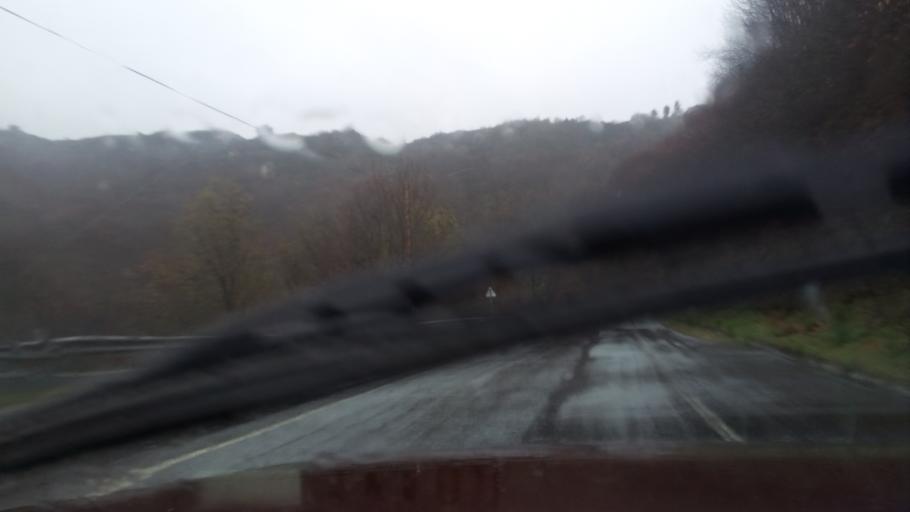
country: PT
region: Guarda
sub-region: Guarda
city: Guarda
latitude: 40.5501
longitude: -7.3156
